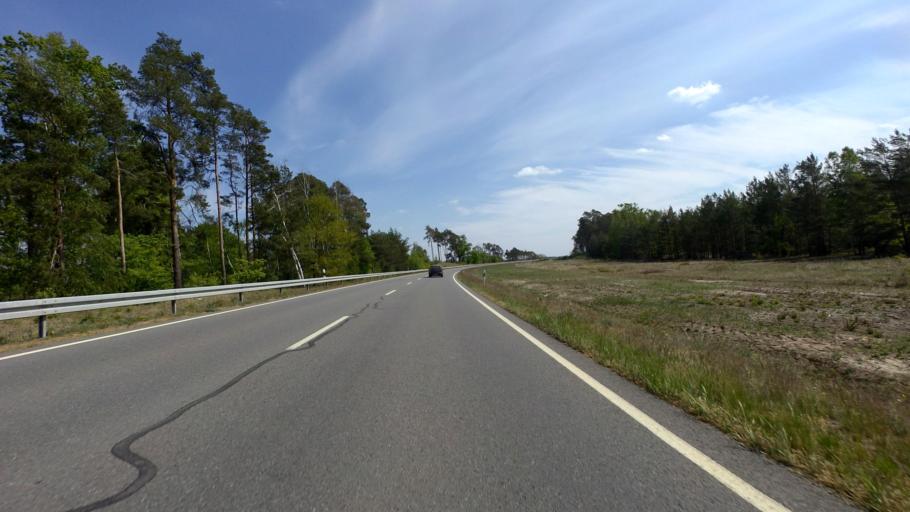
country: DE
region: Brandenburg
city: Cottbus
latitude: 51.7830
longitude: 14.3839
